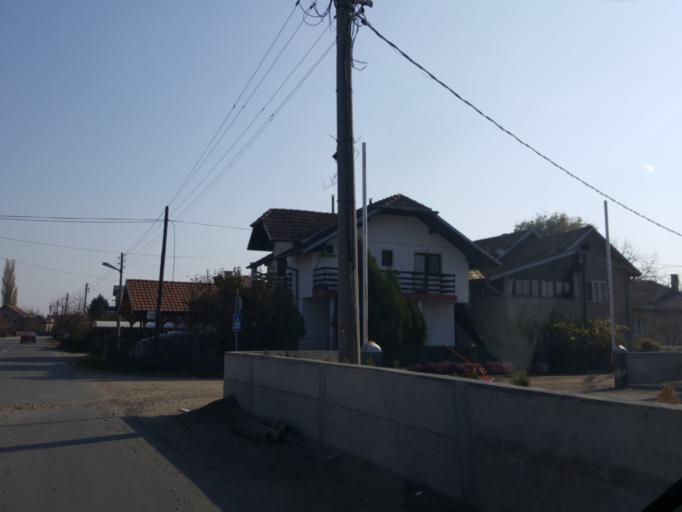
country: RS
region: Central Serbia
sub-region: Borski Okrug
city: Negotin
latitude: 44.2282
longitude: 22.5402
